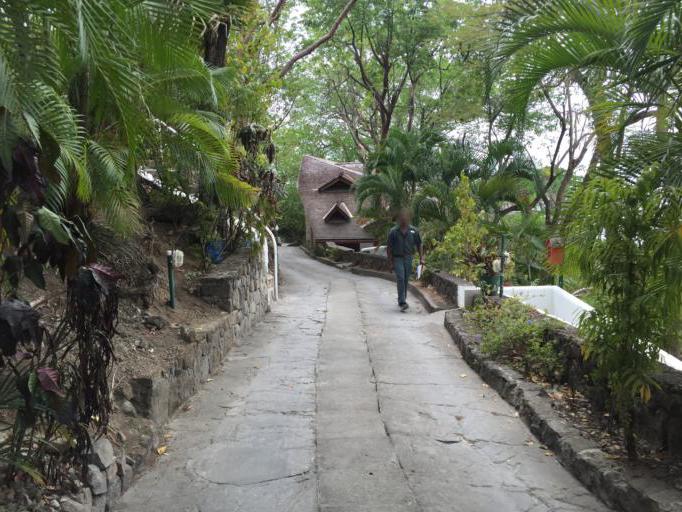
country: LC
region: Soufriere
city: Soufriere
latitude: 13.8650
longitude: -61.0765
